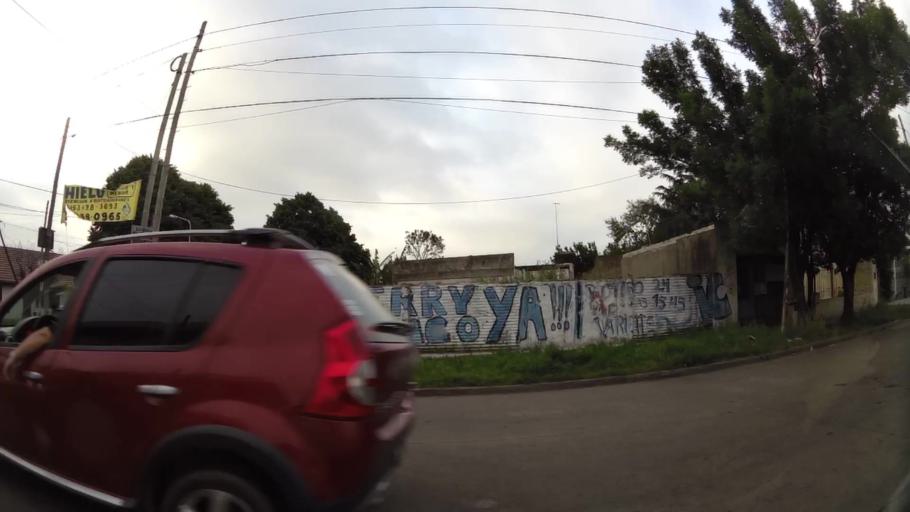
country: AR
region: Buenos Aires
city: San Justo
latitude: -34.6492
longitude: -58.5804
